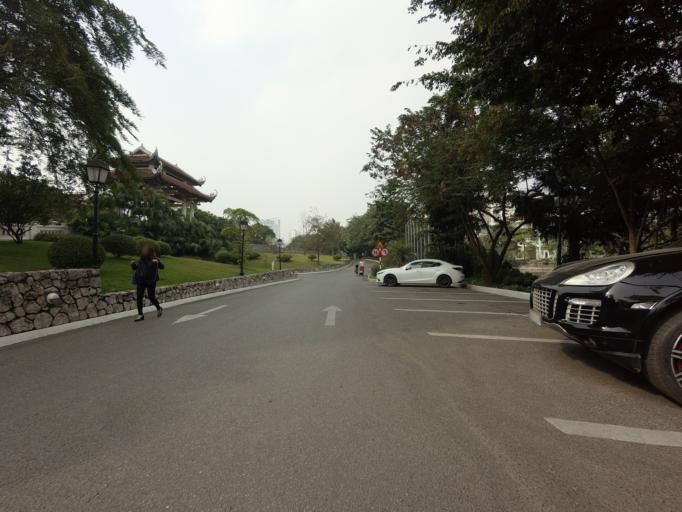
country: VN
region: Ha Noi
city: Tay Ho
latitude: 21.0599
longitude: 105.8321
